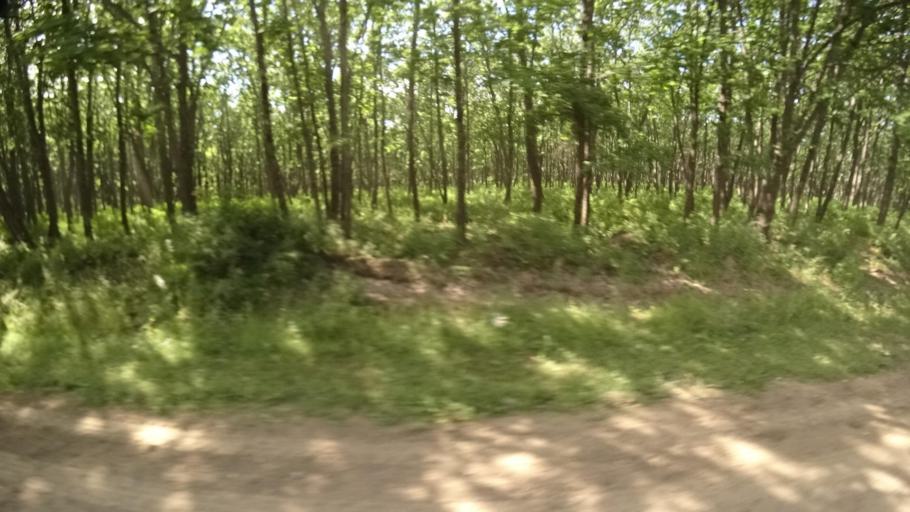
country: RU
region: Primorskiy
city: Yakovlevka
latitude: 44.4081
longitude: 133.5691
